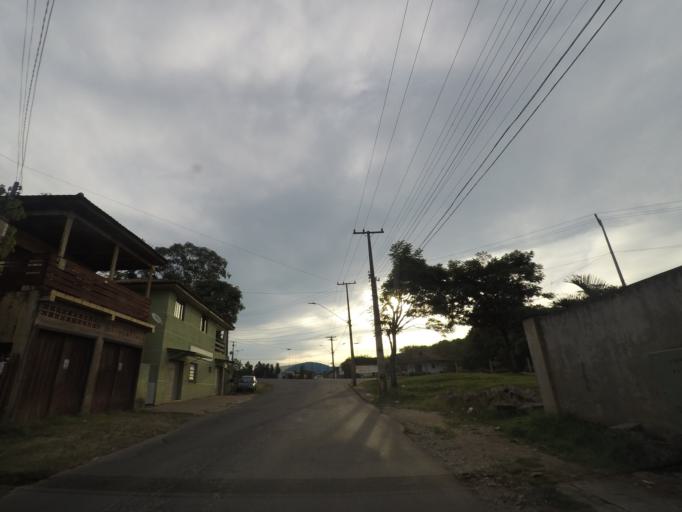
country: BR
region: Parana
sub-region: Colombo
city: Colombo
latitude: -25.2890
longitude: -49.2167
